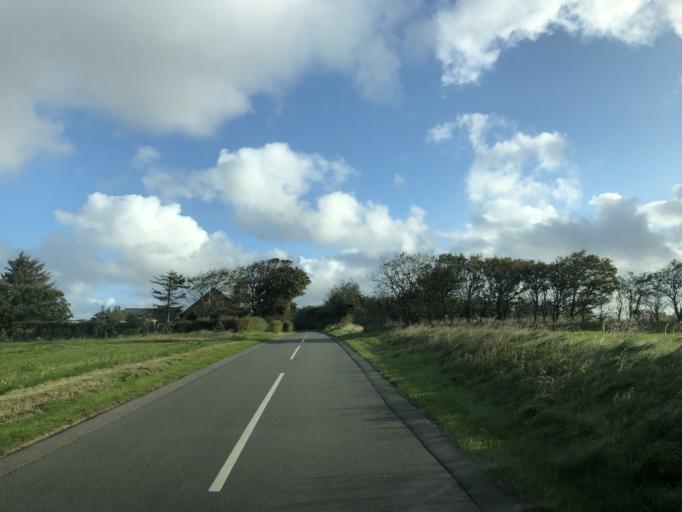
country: DK
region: Central Jutland
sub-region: Holstebro Kommune
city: Ulfborg
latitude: 56.3859
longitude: 8.3481
